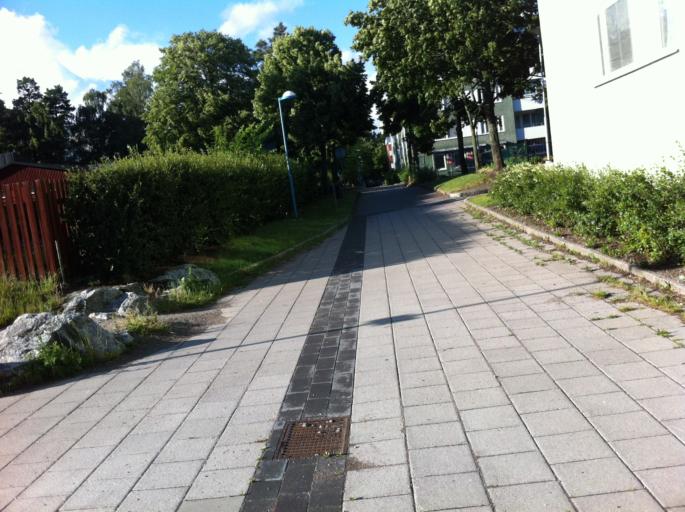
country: SE
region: Stockholm
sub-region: Stockholms Kommun
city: Kista
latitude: 59.3892
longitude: 17.9320
